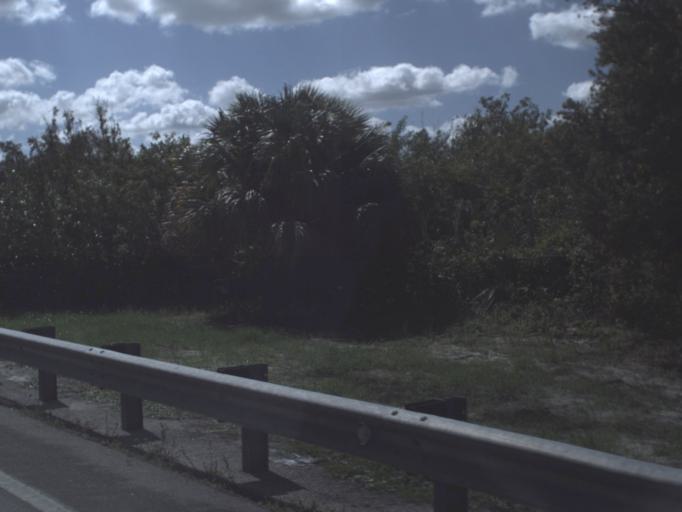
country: US
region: Florida
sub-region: Collier County
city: Marco
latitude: 25.9787
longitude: -81.5592
